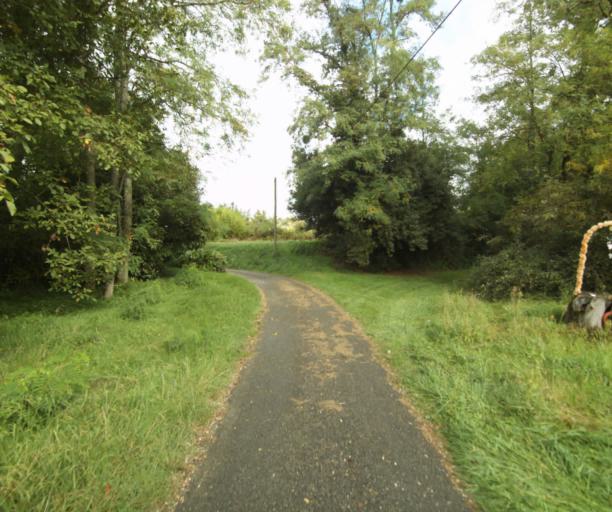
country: FR
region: Midi-Pyrenees
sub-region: Departement du Gers
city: Le Houga
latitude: 43.8349
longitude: -0.0983
